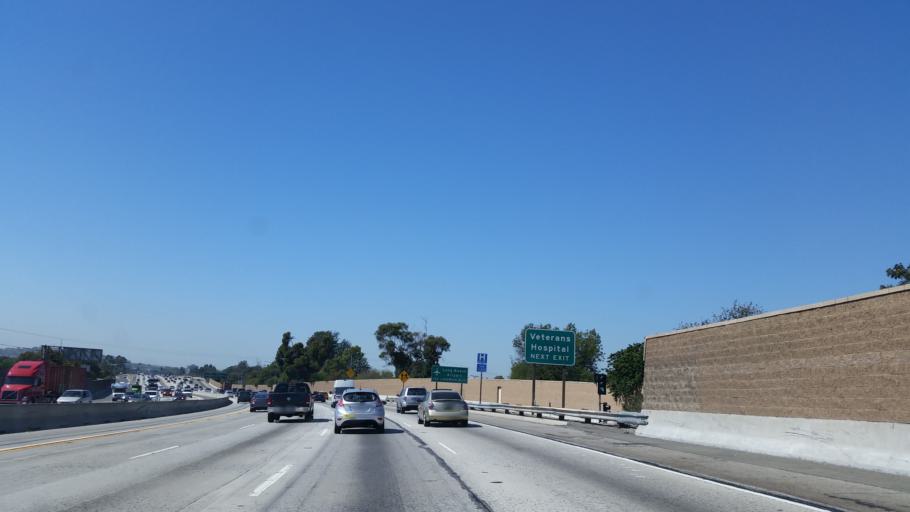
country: US
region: California
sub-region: Orange County
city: Rossmoor
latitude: 33.8025
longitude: -118.1161
